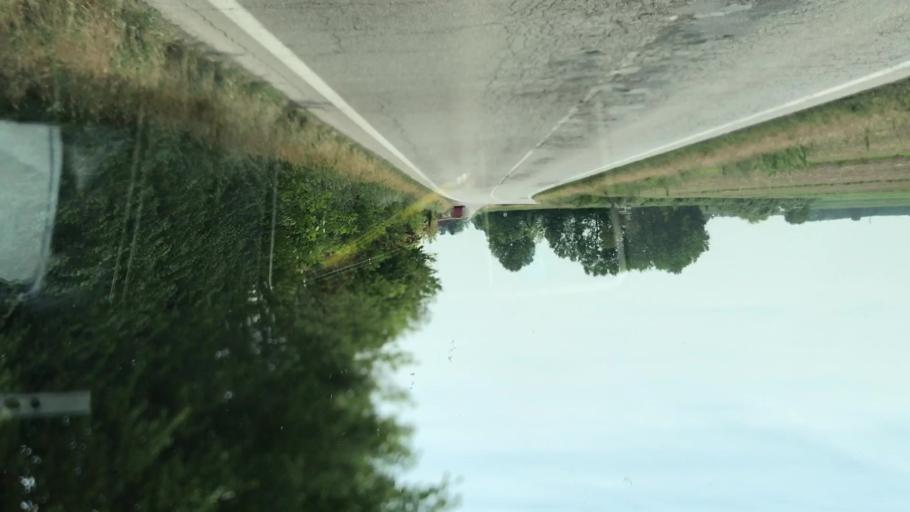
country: IT
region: Lombardy
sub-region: Provincia di Mantova
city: Campitello
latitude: 45.0760
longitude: 10.5919
